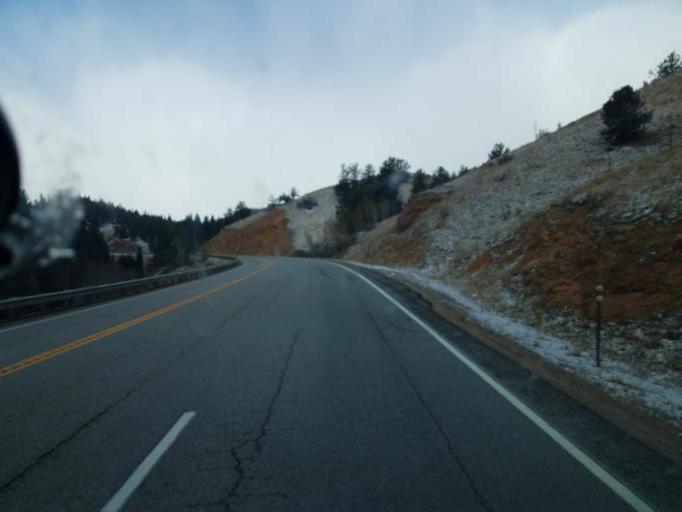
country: US
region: Colorado
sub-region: Clear Creek County
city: Georgetown
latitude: 39.4479
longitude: -105.7358
